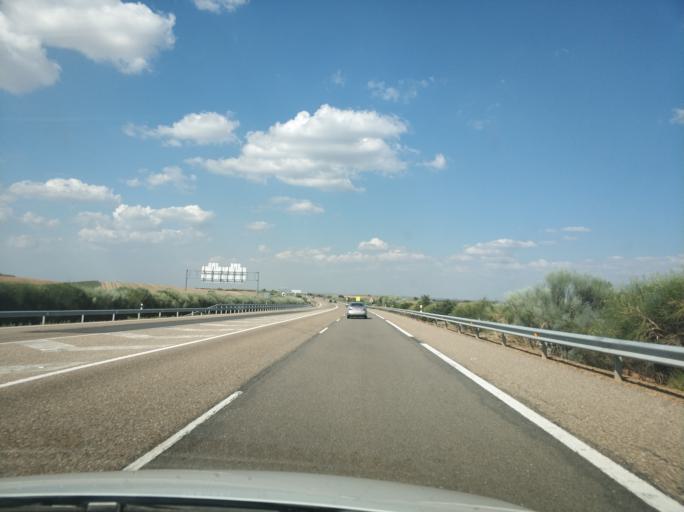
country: ES
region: Castille and Leon
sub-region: Provincia de Zamora
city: San Cristobal de Entrevinas
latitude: 42.0633
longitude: -5.6680
